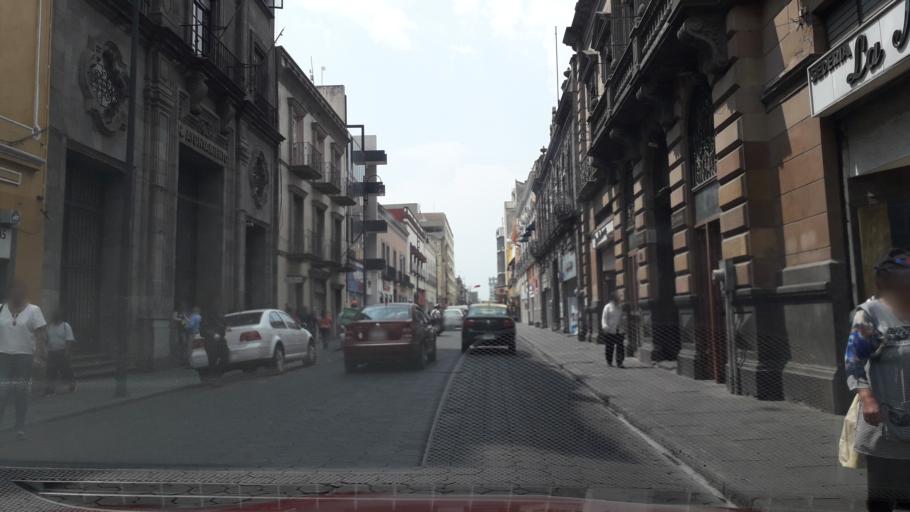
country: MX
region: Puebla
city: Puebla
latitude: 19.0454
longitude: -98.1986
